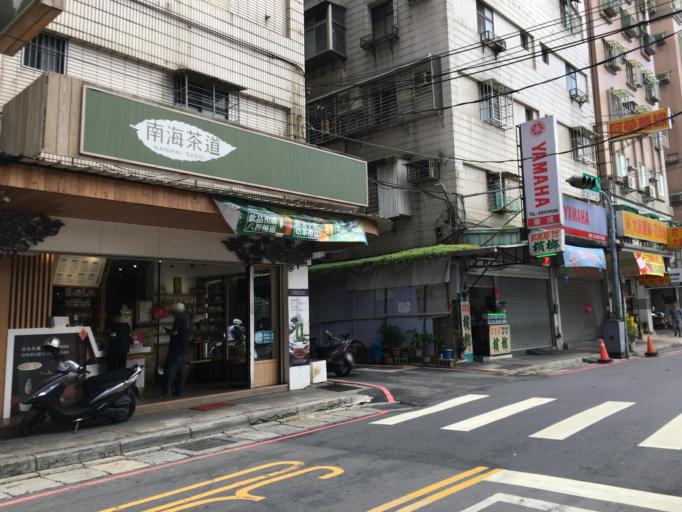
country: TW
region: Taipei
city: Taipei
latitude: 25.0861
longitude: 121.4891
